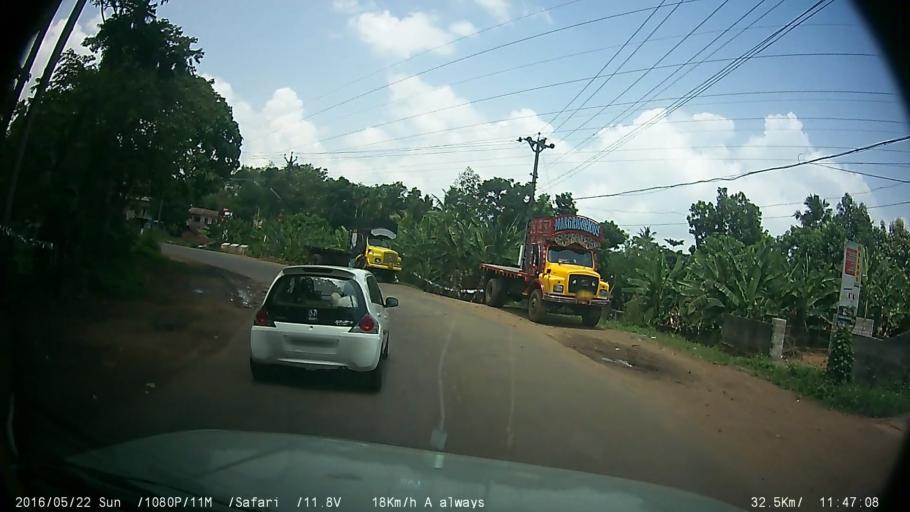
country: IN
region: Kerala
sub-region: Kottayam
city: Kottayam
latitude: 9.5318
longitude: 76.5233
